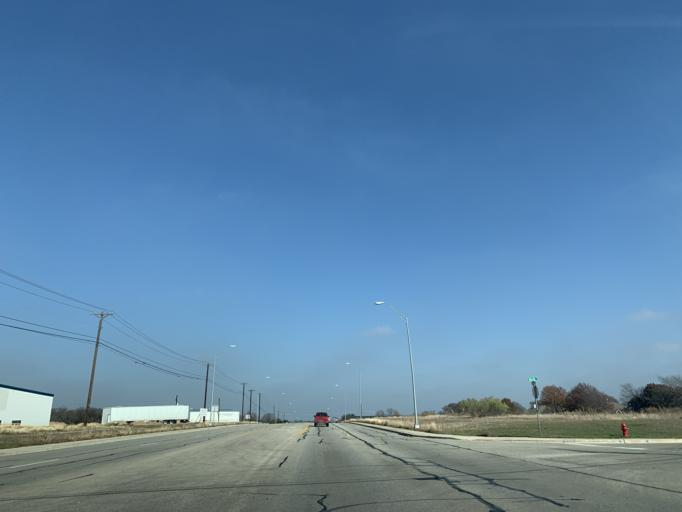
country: US
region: Texas
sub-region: Williamson County
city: Round Rock
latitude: 30.5248
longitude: -97.6539
